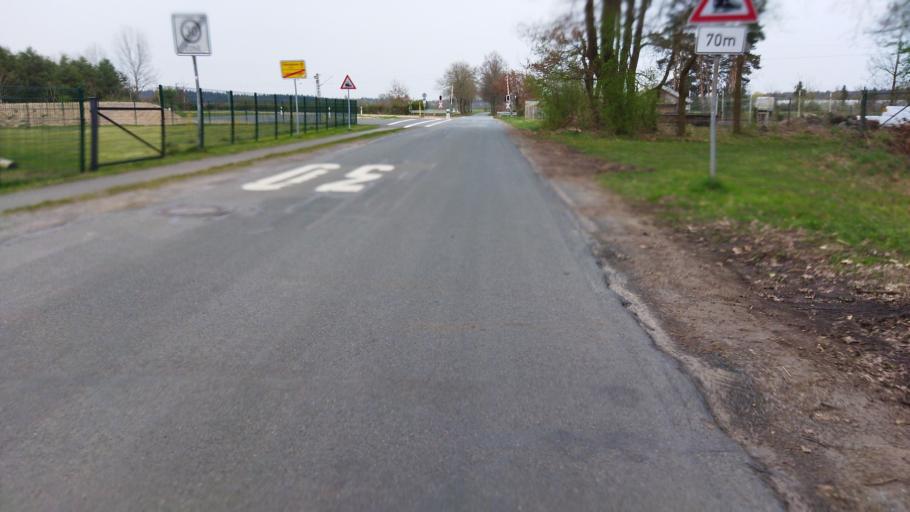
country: DE
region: Lower Saxony
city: Estorf
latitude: 52.5969
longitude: 9.1660
